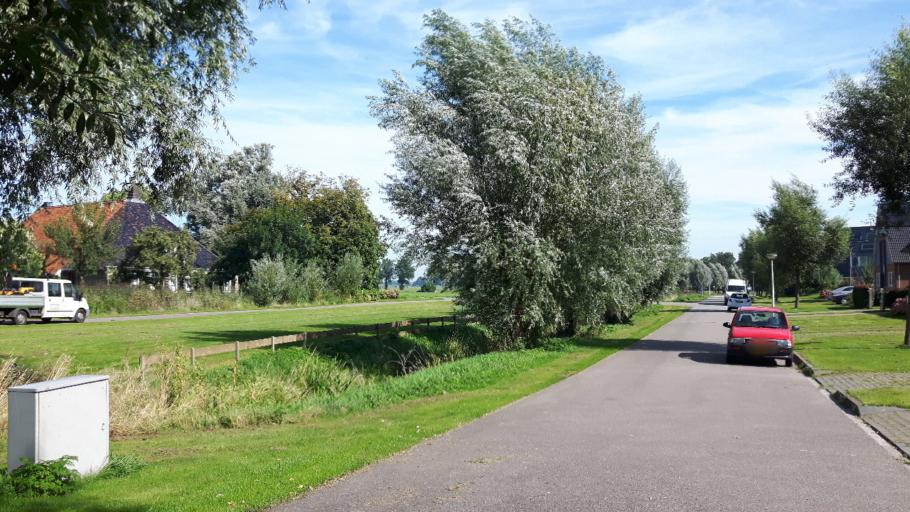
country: NL
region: Friesland
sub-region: Gemeente Skarsterlan
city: Joure
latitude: 53.0138
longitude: 5.7746
